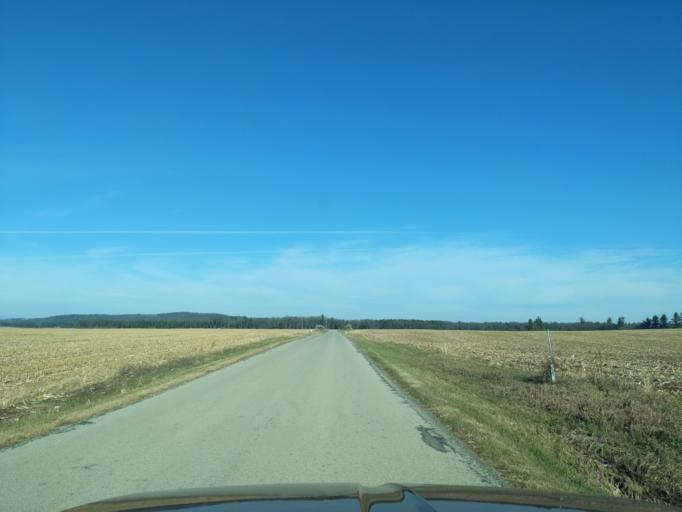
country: US
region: Wisconsin
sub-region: Waushara County
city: Silver Lake
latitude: 44.0909
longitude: -89.1739
